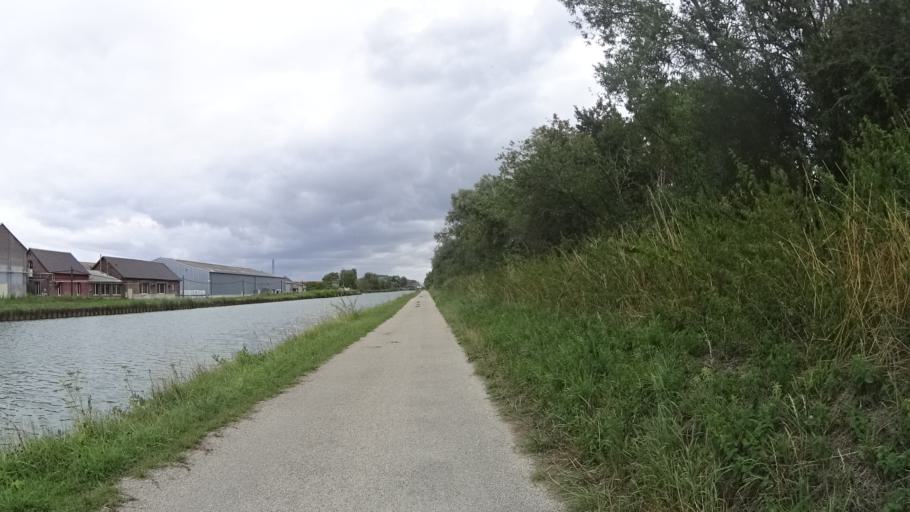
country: FR
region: Picardie
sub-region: Departement de l'Aisne
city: Chauny
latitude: 49.6126
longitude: 3.2341
